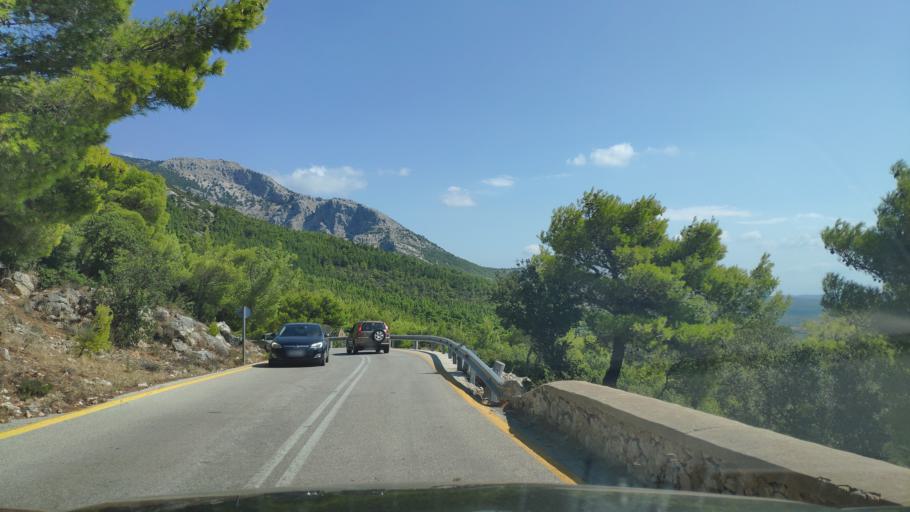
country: GR
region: Attica
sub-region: Nomarchia Anatolikis Attikis
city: Thrakomakedones
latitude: 38.1357
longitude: 23.7288
